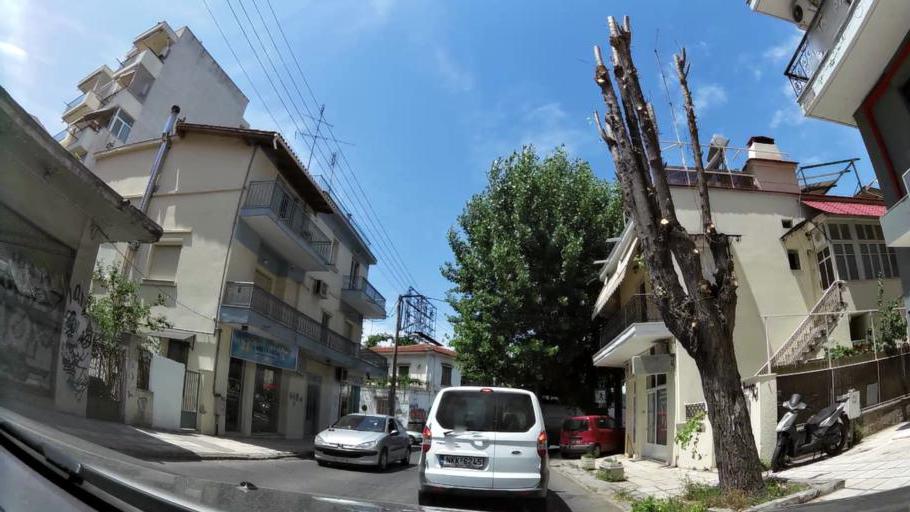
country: GR
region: Central Macedonia
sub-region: Nomos Thessalonikis
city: Triandria
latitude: 40.6215
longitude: 22.9681
